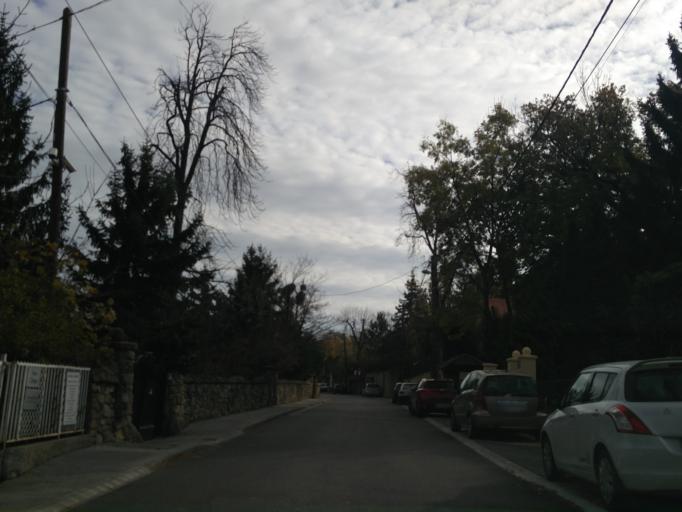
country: HU
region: Budapest
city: Budapest XII. keruelet
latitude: 47.5005
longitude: 18.9859
